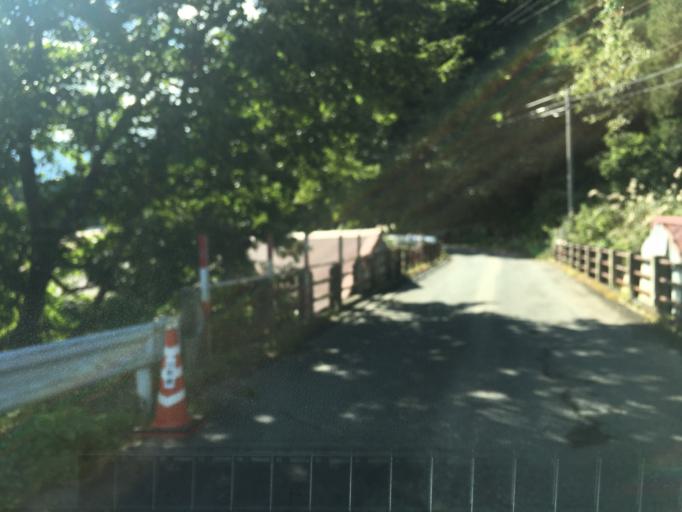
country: JP
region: Yamagata
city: Yonezawa
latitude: 37.8125
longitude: 140.2703
